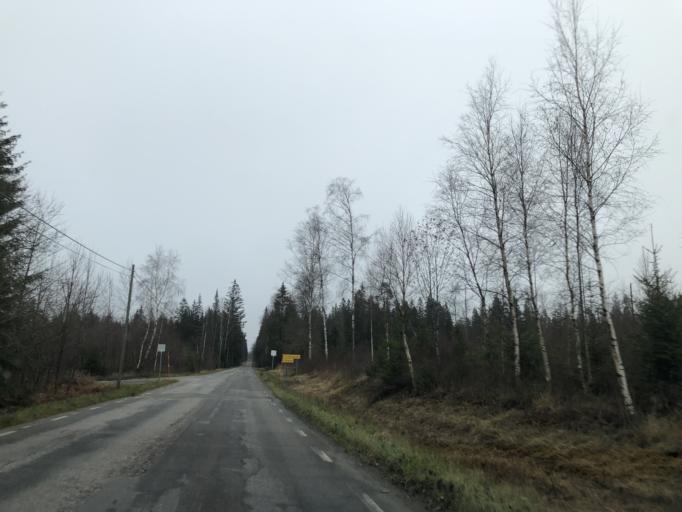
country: SE
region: Vaestra Goetaland
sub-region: Ulricehamns Kommun
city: Ulricehamn
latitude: 57.7051
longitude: 13.5032
